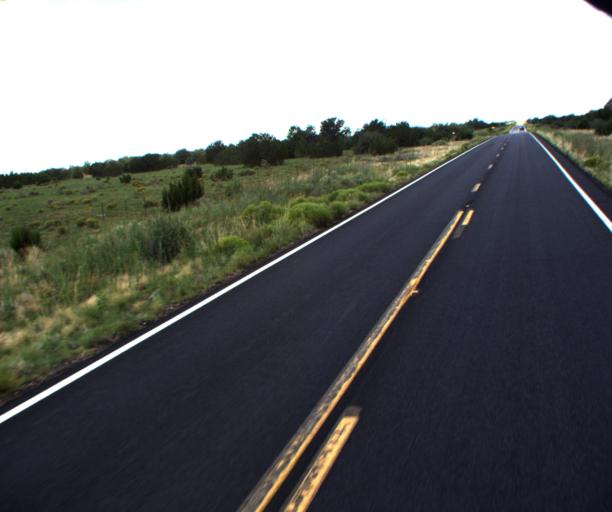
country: US
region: Arizona
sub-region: Coconino County
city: Parks
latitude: 35.6076
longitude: -112.0525
